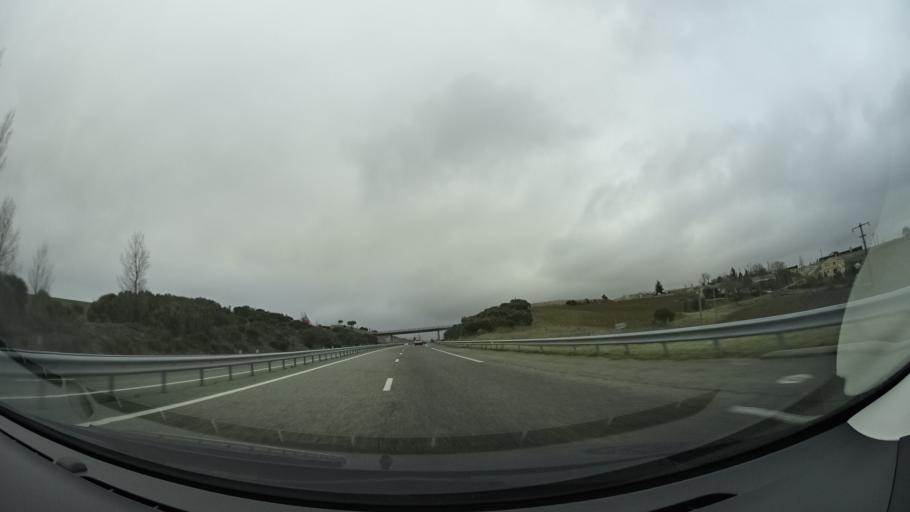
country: FR
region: Midi-Pyrenees
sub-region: Departement de la Haute-Garonne
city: Nailloux
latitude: 43.3800
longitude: 1.6114
